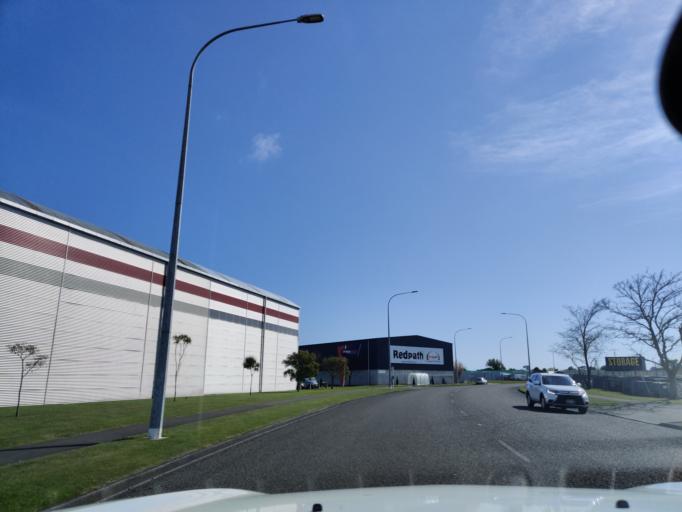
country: NZ
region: Manawatu-Wanganui
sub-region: Palmerston North City
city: Palmerston North
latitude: -40.3351
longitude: 175.6446
